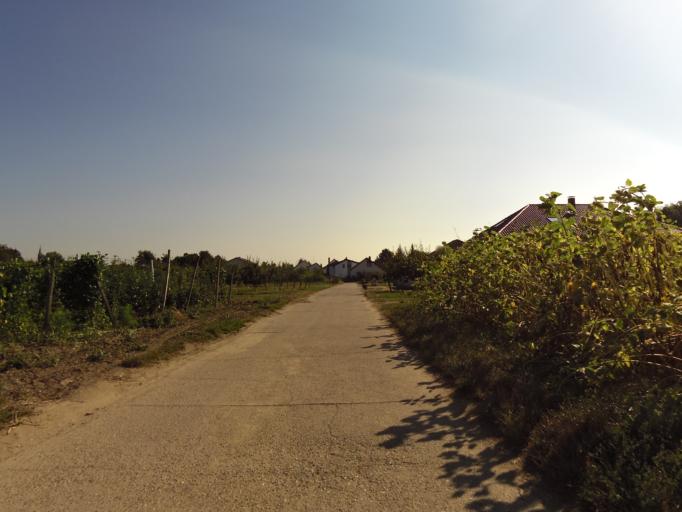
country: DE
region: Rheinland-Pfalz
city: Weisenheim am Sand
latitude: 49.5136
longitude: 8.2411
